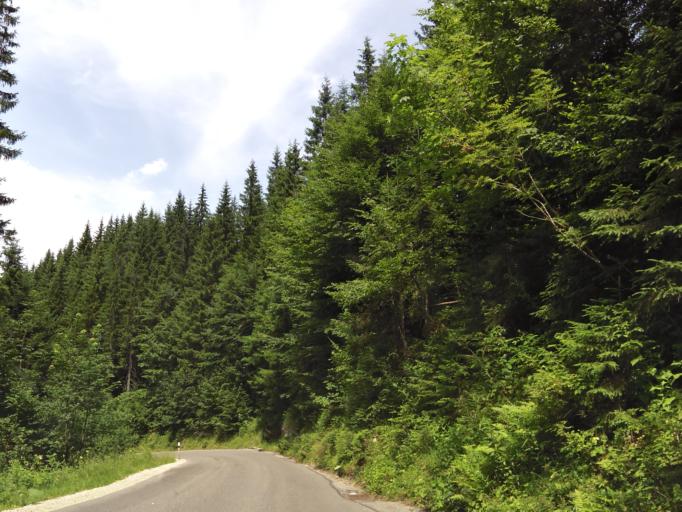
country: AT
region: Tyrol
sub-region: Politischer Bezirk Kitzbuhel
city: Waidring
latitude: 47.6592
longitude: 12.5753
